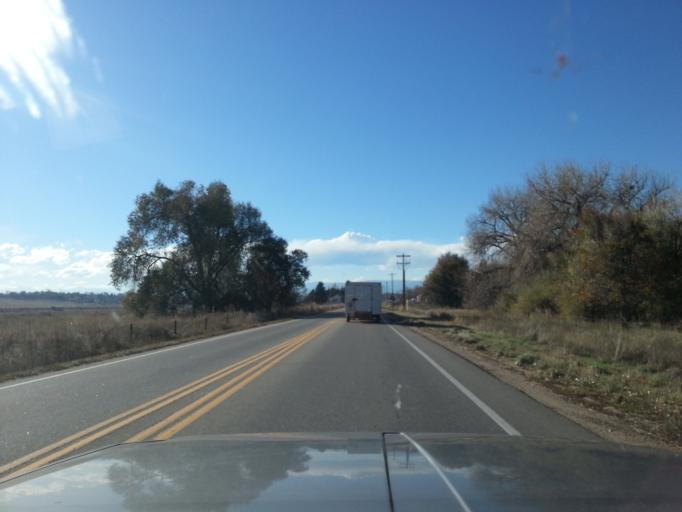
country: US
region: Colorado
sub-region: Larimer County
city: Loveland
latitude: 40.3784
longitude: -105.0581
